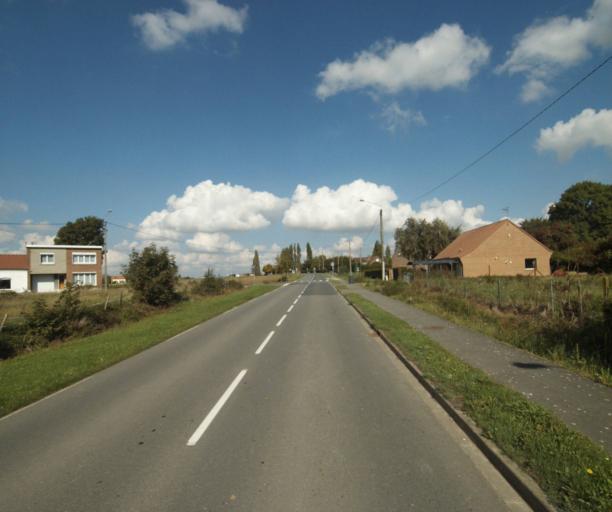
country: FR
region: Nord-Pas-de-Calais
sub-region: Departement du Nord
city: Illies
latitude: 50.5748
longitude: 2.8228
